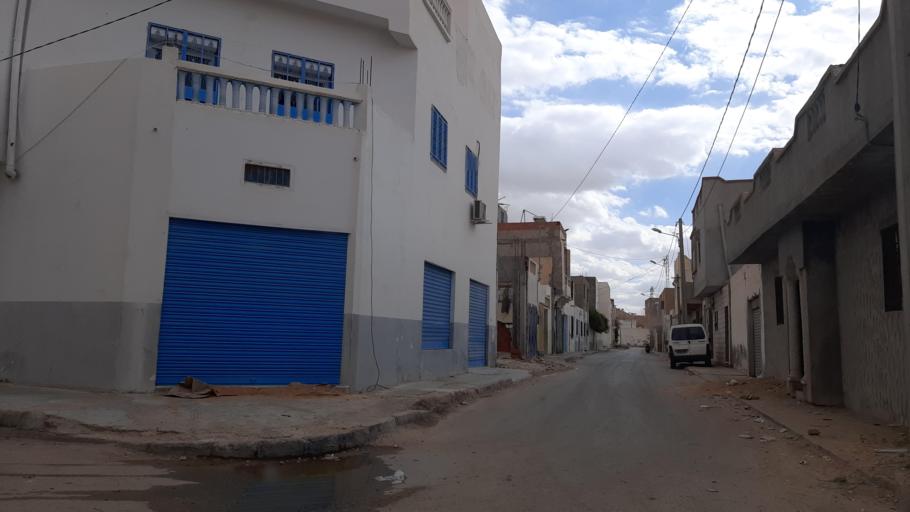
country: TN
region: Tataouine
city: Tataouine
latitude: 32.9379
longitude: 10.4511
